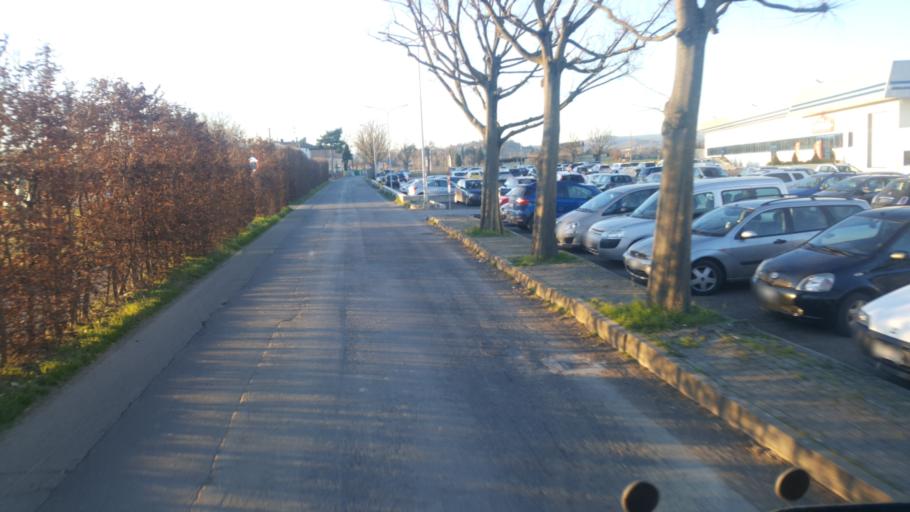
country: IT
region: Emilia-Romagna
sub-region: Provincia di Modena
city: Ca' di Sola
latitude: 44.5371
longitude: 10.9690
